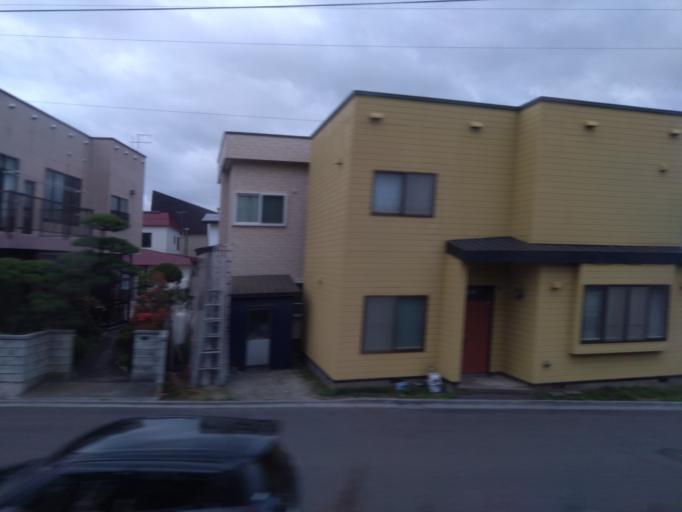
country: JP
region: Hokkaido
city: Hakodate
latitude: 41.7916
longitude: 140.7309
